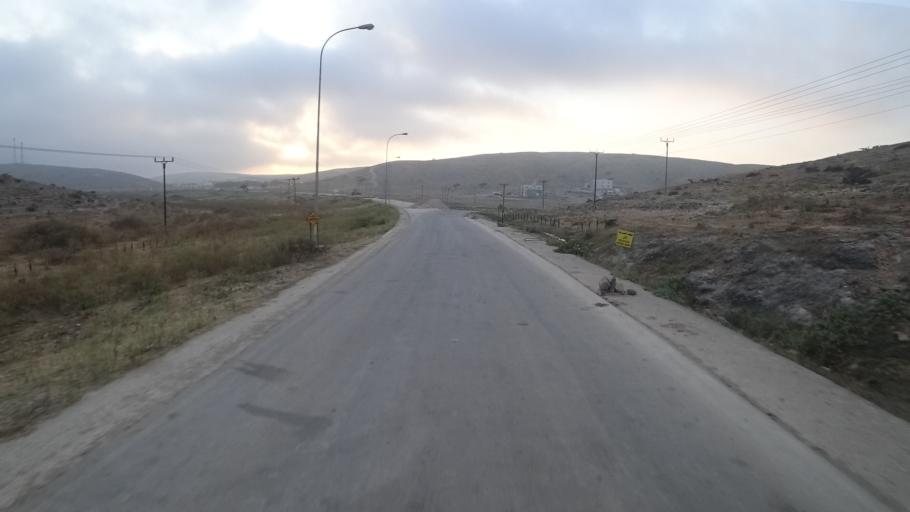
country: OM
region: Zufar
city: Salalah
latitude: 17.1267
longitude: 53.9462
